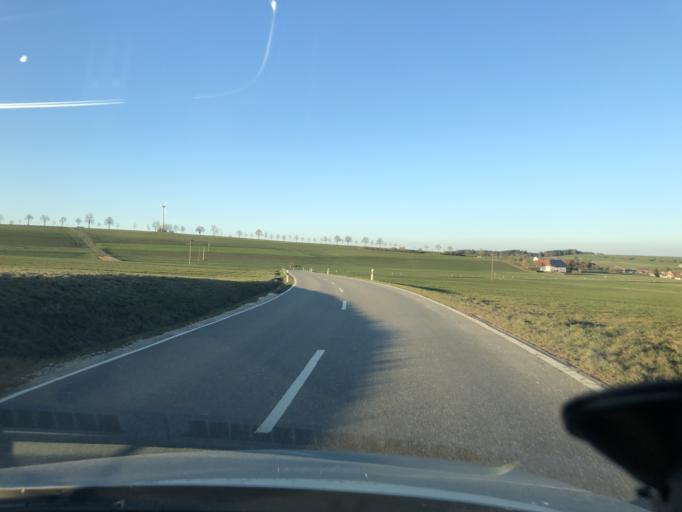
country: DE
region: Baden-Wuerttemberg
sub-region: Freiburg Region
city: Hufingen
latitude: 47.8860
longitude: 8.4762
